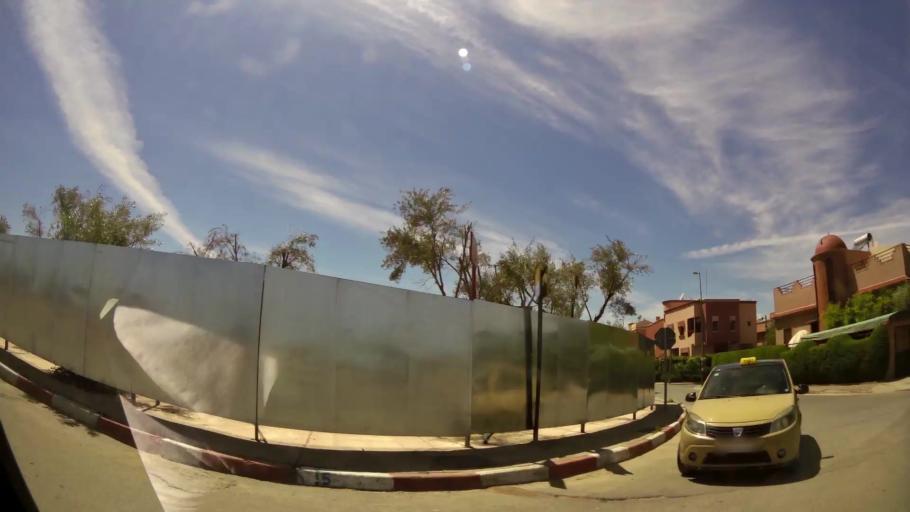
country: MA
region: Marrakech-Tensift-Al Haouz
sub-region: Marrakech
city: Marrakesh
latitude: 31.6734
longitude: -7.9992
